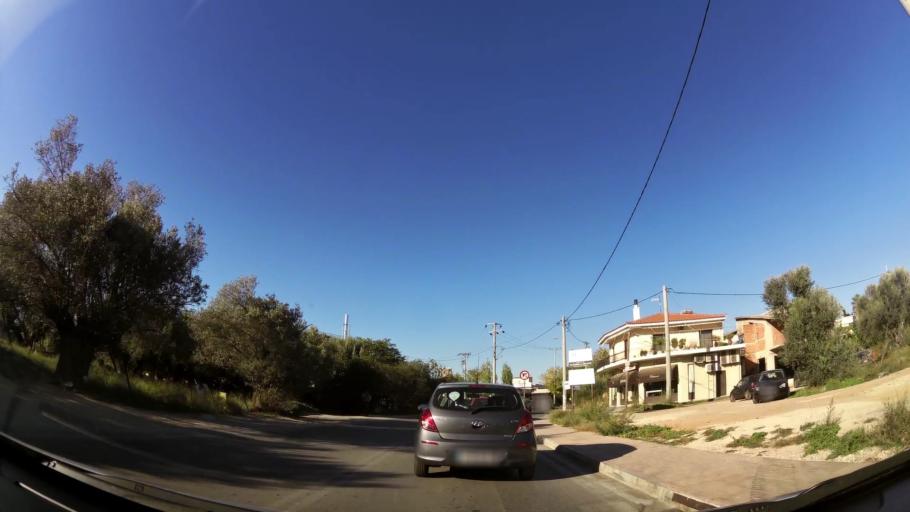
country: GR
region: Attica
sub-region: Nomarchia Athinas
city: Lykovrysi
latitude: 38.0775
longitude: 23.7943
